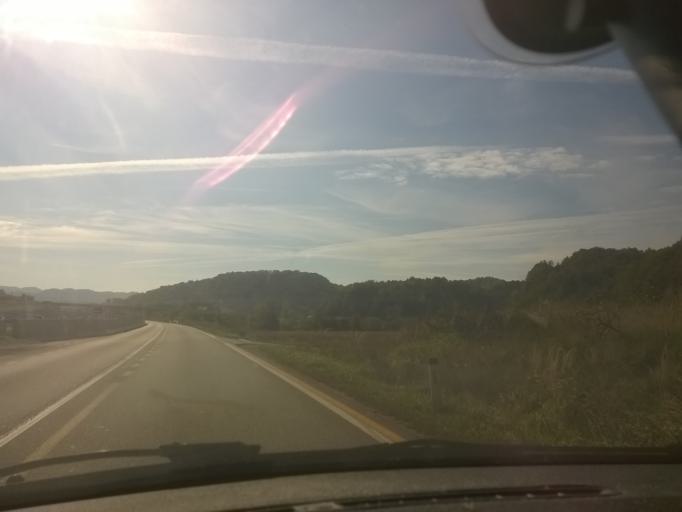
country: SI
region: Podlehnik
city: Podlehnik
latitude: 46.3518
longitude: 15.8681
